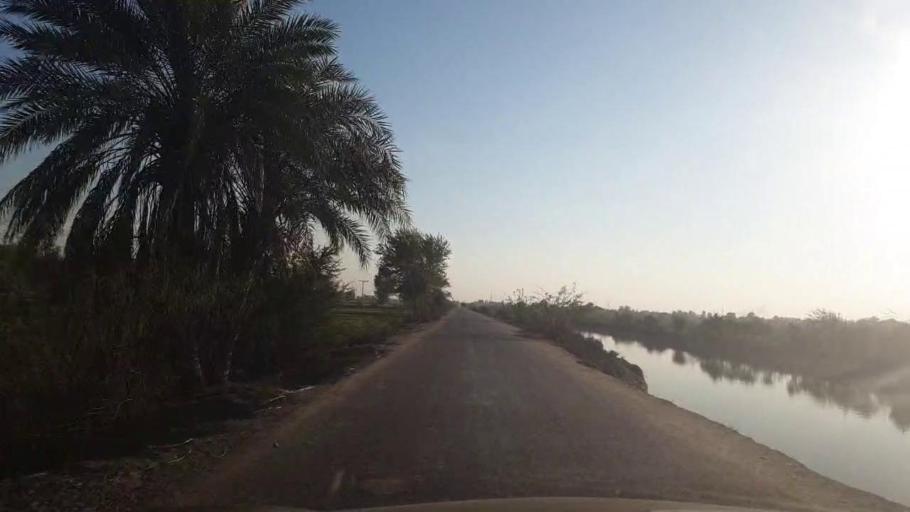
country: PK
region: Sindh
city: Mirpur Mathelo
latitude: 28.0050
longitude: 69.4695
